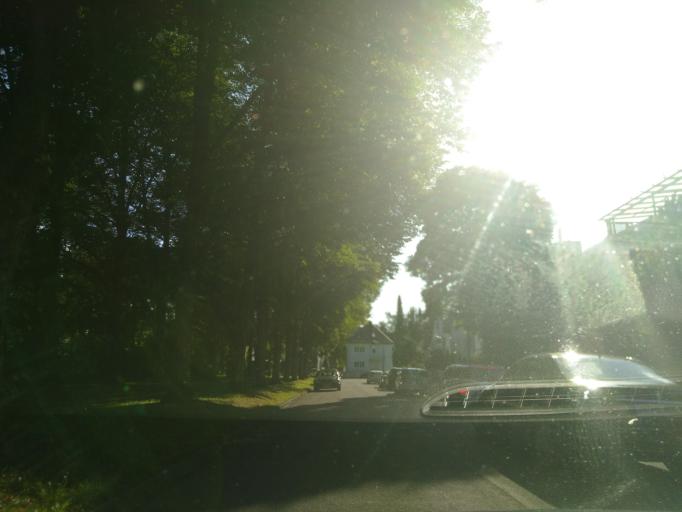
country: DE
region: Bavaria
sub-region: Upper Bavaria
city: Munich
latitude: 48.0906
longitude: 11.5666
